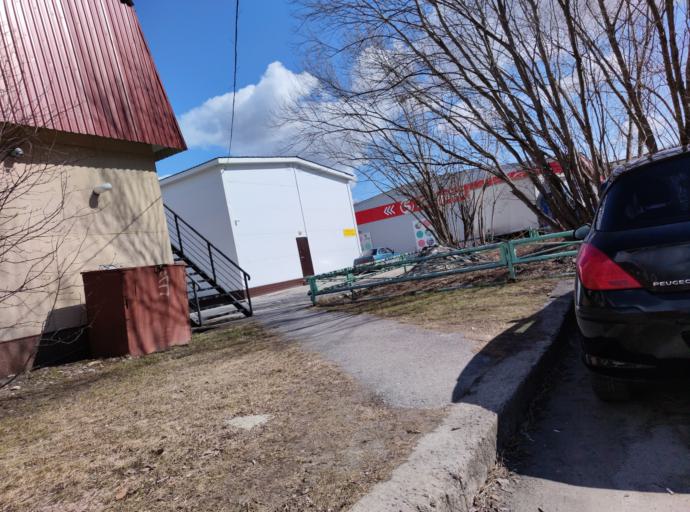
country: RU
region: Khanty-Mansiyskiy Avtonomnyy Okrug
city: Langepas
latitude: 61.2526
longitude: 75.1727
